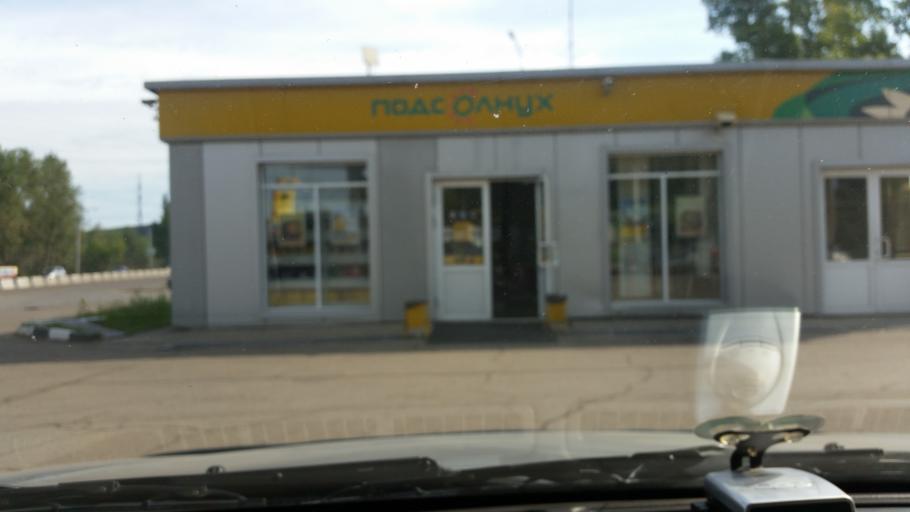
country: RU
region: Irkutsk
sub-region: Irkutskiy Rayon
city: Irkutsk
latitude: 52.3320
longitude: 104.3175
